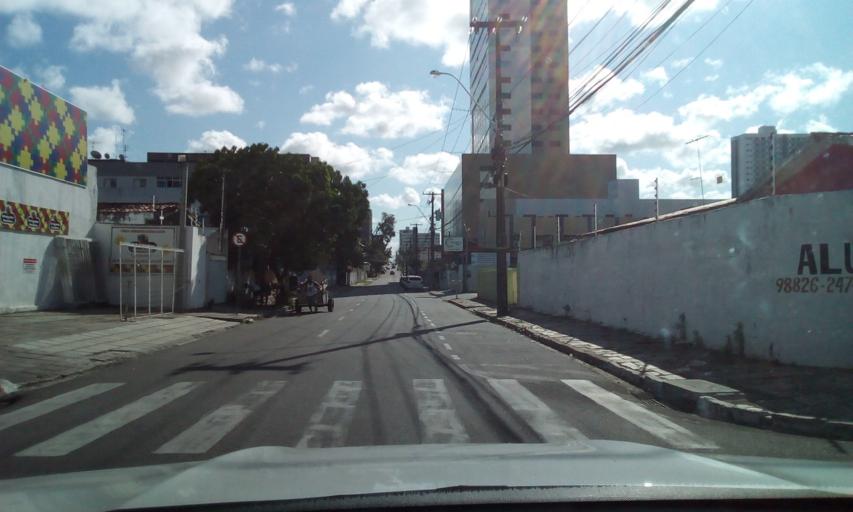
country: BR
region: Paraiba
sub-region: Joao Pessoa
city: Joao Pessoa
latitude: -7.1186
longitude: -34.8552
